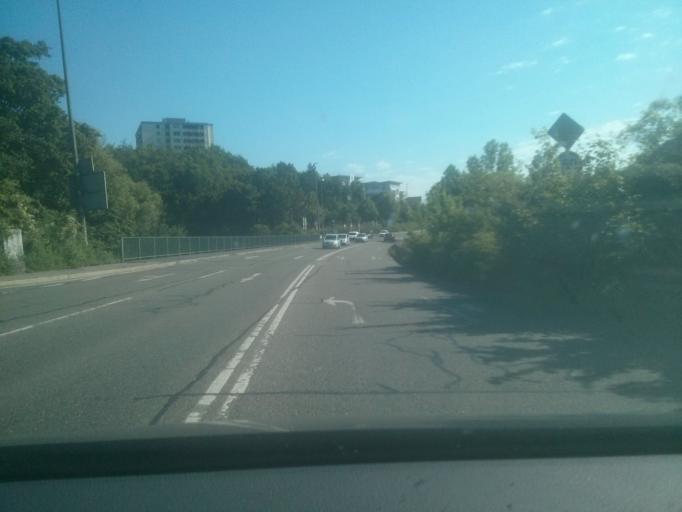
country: DE
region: Baden-Wuerttemberg
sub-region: Tuebingen Region
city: Wannweil
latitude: 48.4961
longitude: 9.1647
